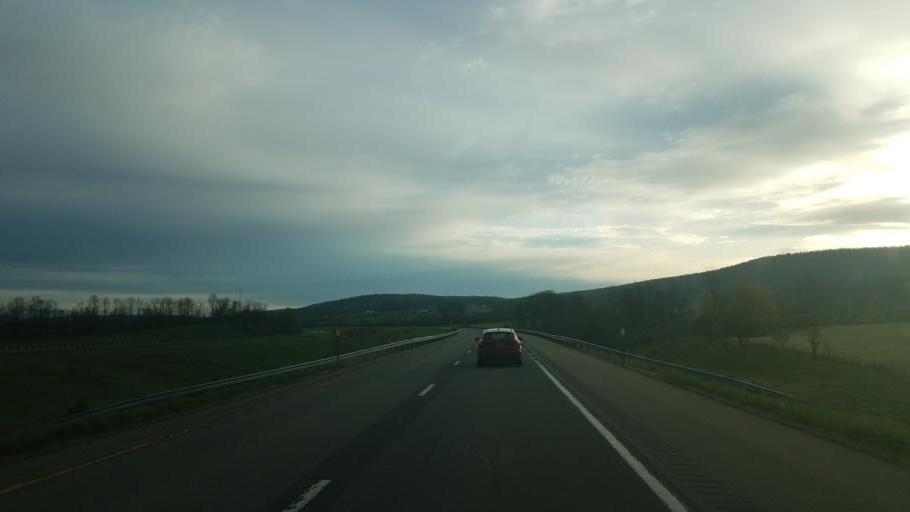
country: US
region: New York
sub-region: Allegany County
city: Belmont
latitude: 42.2792
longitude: -78.0384
